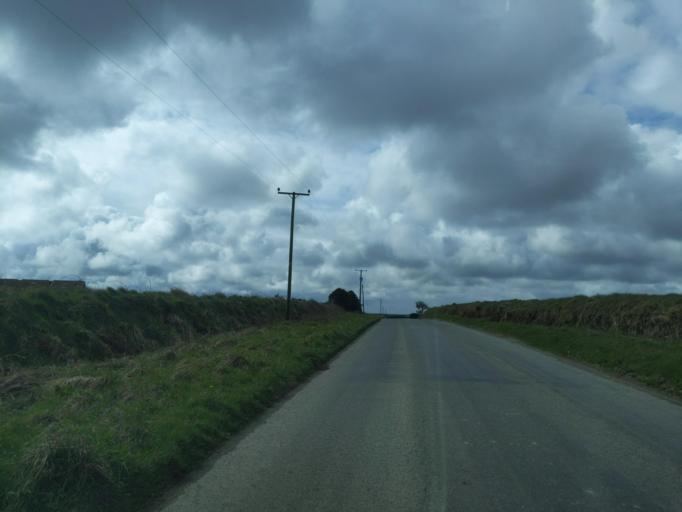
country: GB
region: England
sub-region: Cornwall
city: Camelford
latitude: 50.6410
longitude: -4.6418
